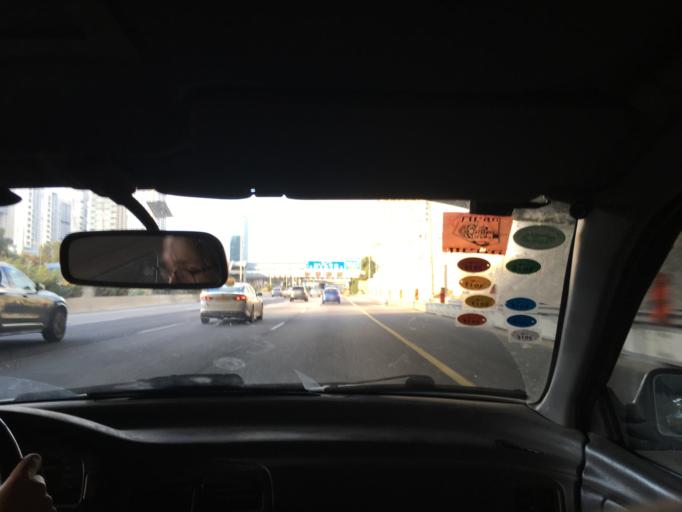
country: IL
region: Tel Aviv
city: Ramat Gan
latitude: 32.0816
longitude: 34.7983
